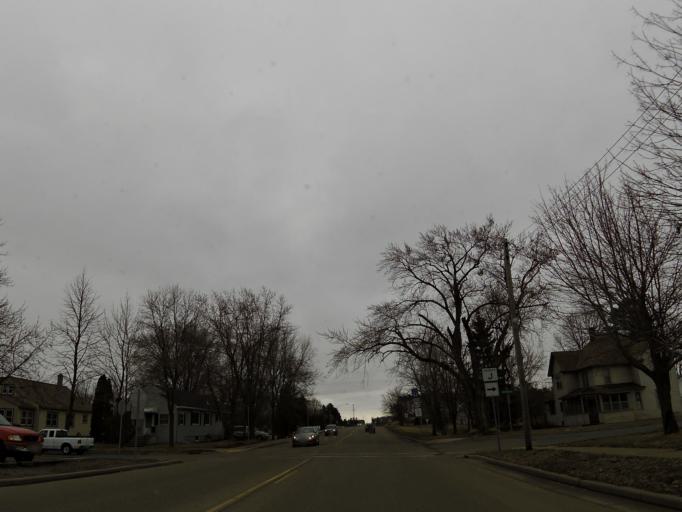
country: US
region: Wisconsin
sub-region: Saint Croix County
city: Baldwin
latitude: 44.9643
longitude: -92.3750
